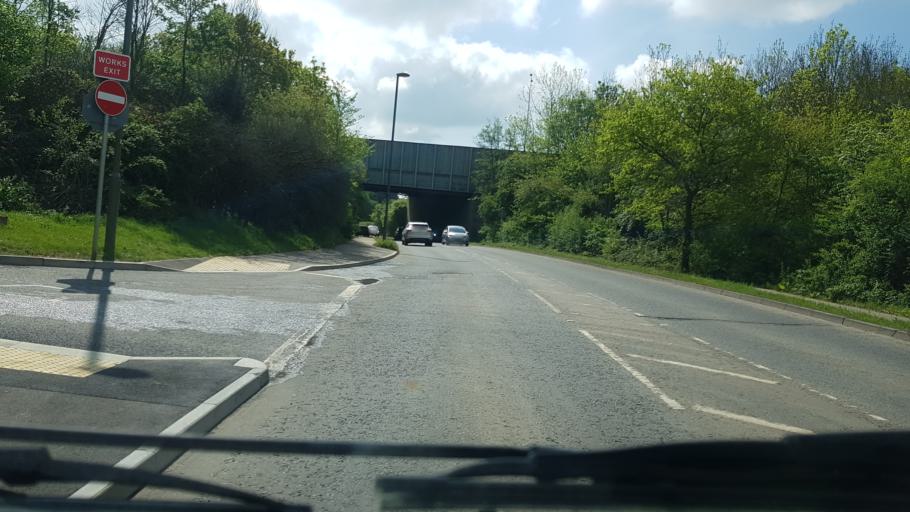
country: GB
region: England
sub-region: Surrey
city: Leatherhead
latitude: 51.3143
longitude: -0.3557
